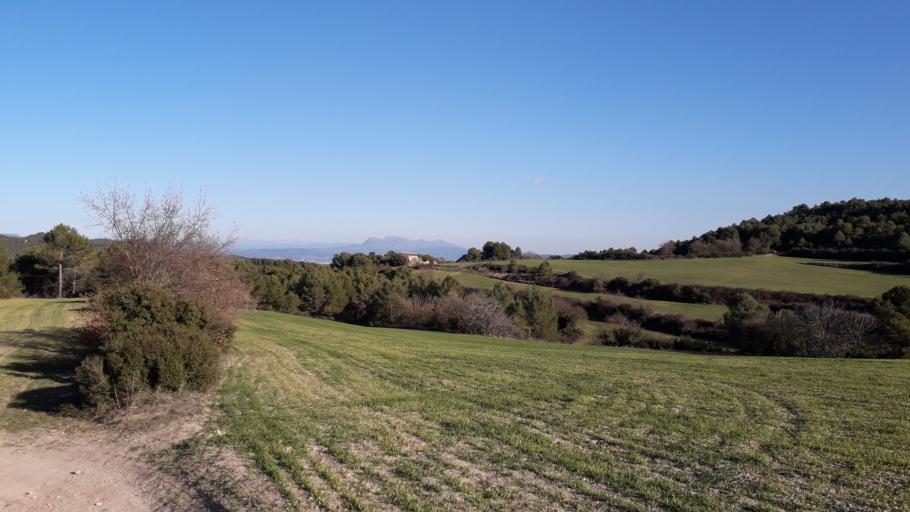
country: ES
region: Catalonia
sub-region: Provincia de Barcelona
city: Bellprat
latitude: 41.5578
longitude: 1.4526
